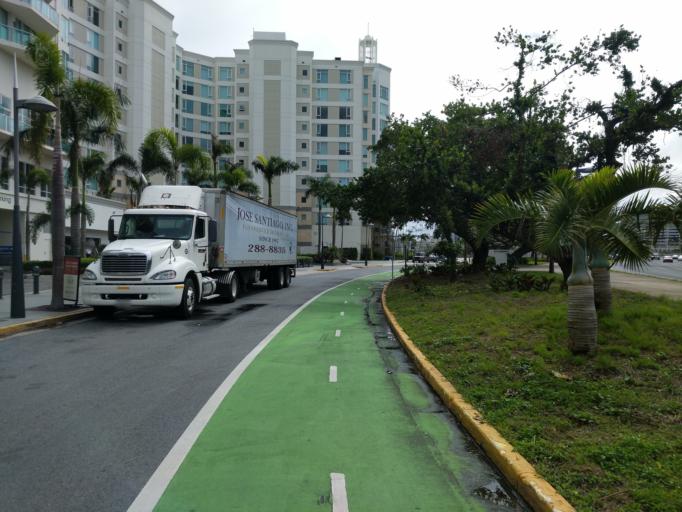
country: PR
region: San Juan
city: San Juan
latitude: 18.4617
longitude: -66.0870
